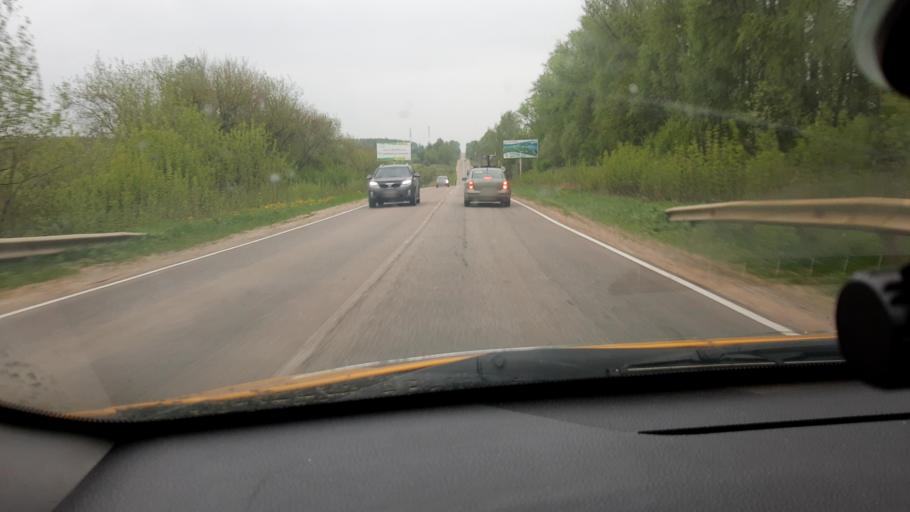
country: RU
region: Tula
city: Zaokskiy
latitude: 54.7823
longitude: 37.4344
